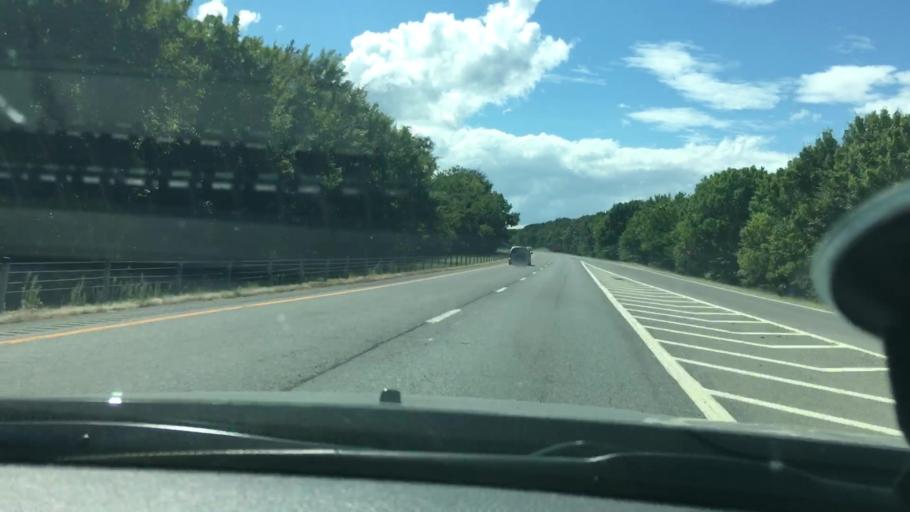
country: US
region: Oklahoma
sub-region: Sequoyah County
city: Vian
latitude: 35.4902
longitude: -95.0821
